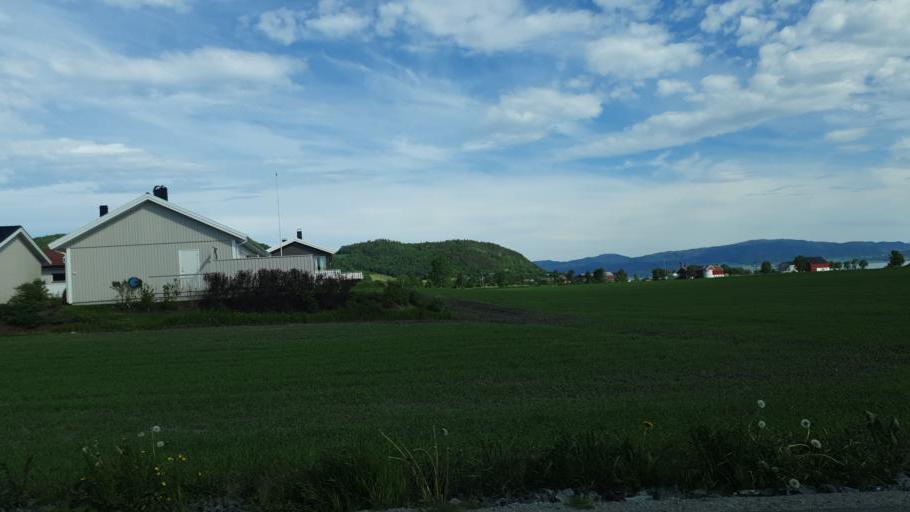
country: NO
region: Sor-Trondelag
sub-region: Rissa
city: Rissa
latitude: 63.5025
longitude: 10.0086
